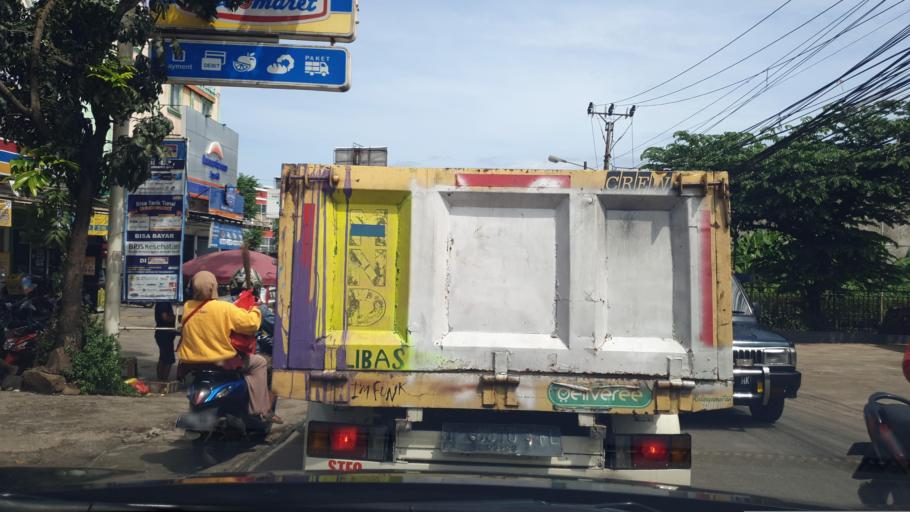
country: ID
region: West Java
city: Sawangan
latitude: -6.4038
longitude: 106.7708
